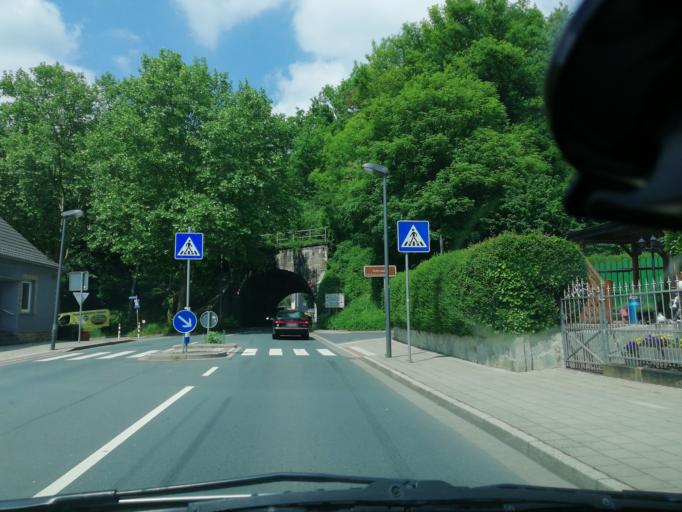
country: DE
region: North Rhine-Westphalia
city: Herdecke
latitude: 51.4010
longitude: 7.4254
